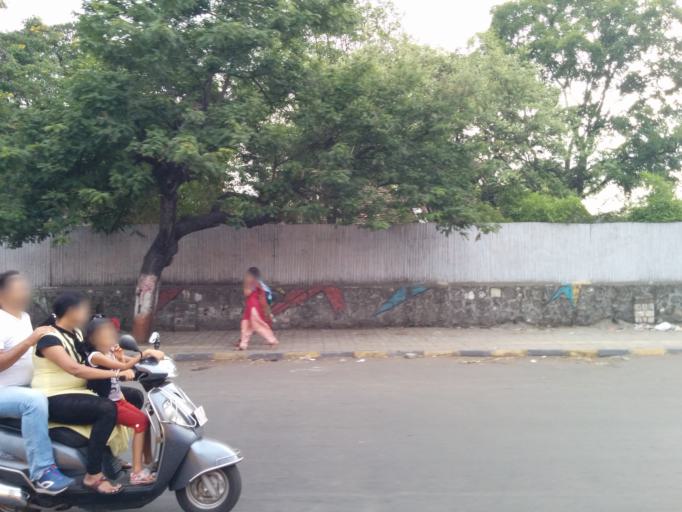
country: IN
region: Maharashtra
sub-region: Pune Division
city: Pune
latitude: 18.5032
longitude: 73.8786
